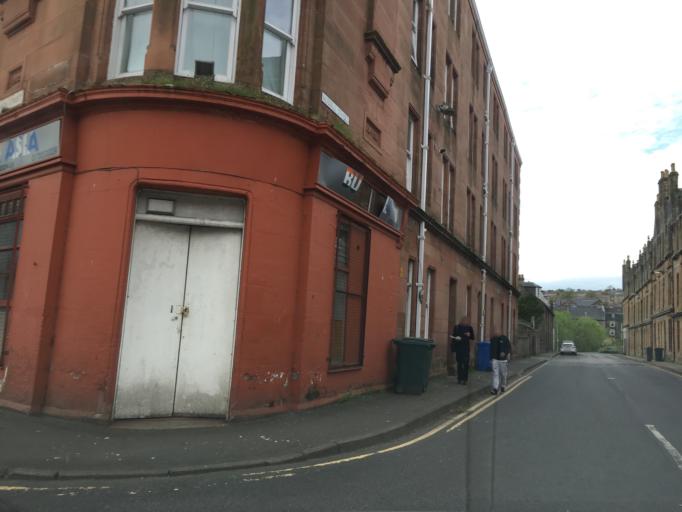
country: GB
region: Scotland
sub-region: Argyll and Bute
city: Rothesay
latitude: 55.8349
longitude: -5.0545
